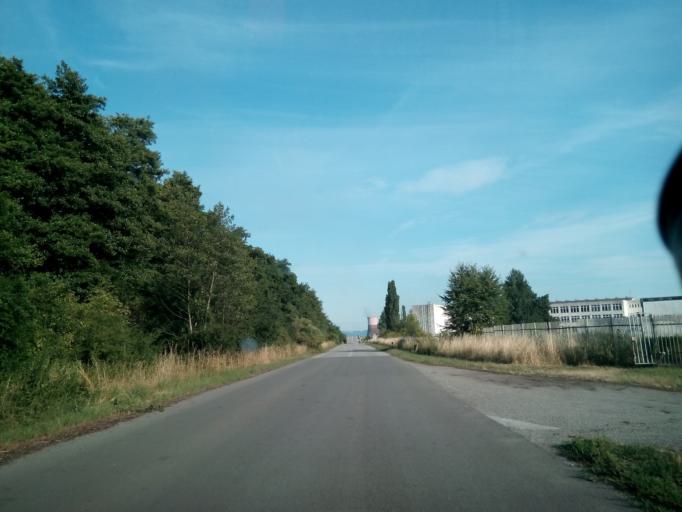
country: SK
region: Kosicky
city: Kosice
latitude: 48.6335
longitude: 21.1779
